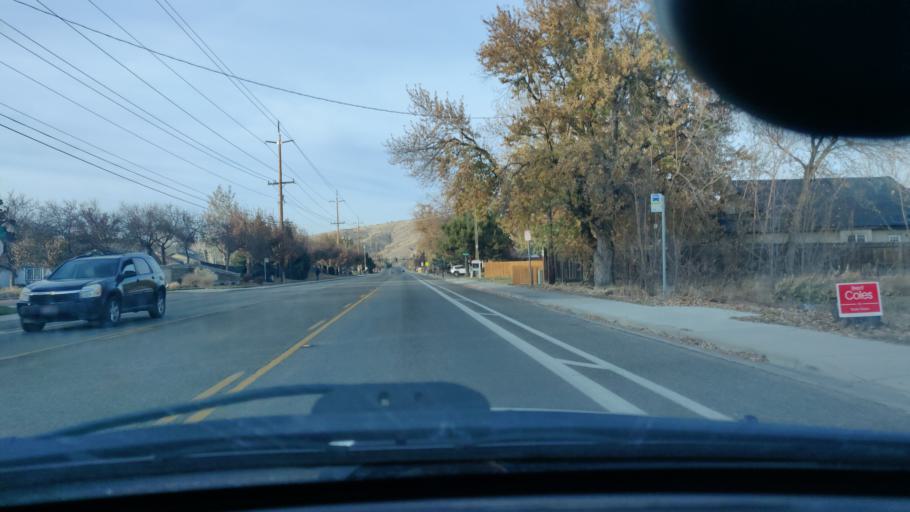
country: US
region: Idaho
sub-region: Ada County
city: Garden City
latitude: 43.6751
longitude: -116.2792
